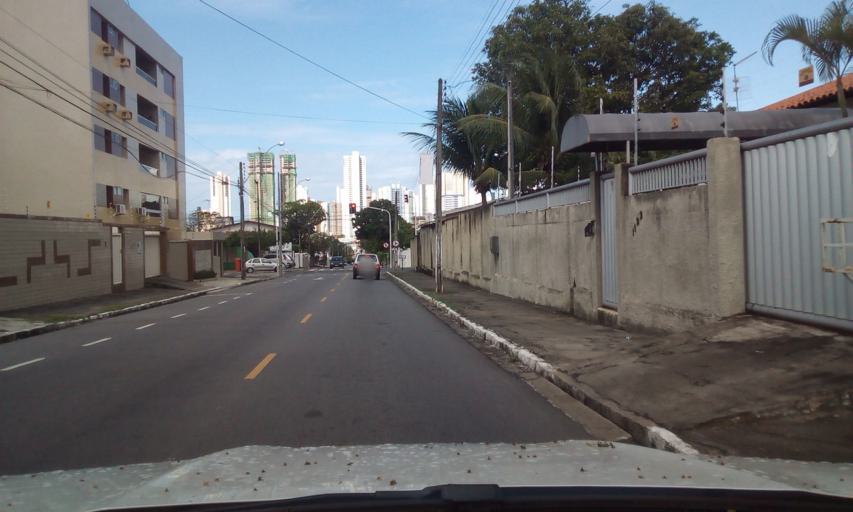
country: BR
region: Paraiba
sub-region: Joao Pessoa
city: Joao Pessoa
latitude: -7.1156
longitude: -34.8501
